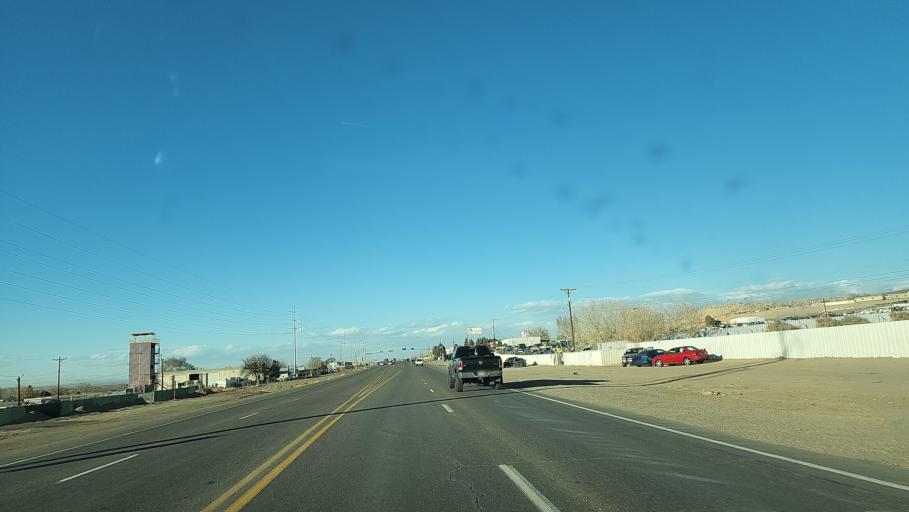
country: US
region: New Mexico
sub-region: Bernalillo County
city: South Valley
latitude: 35.0122
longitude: -106.6489
